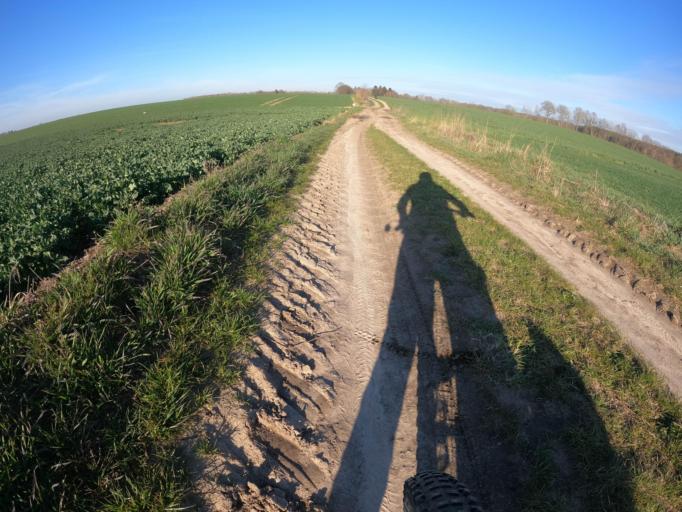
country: PL
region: West Pomeranian Voivodeship
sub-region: Powiat kolobrzeski
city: Ryman
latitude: 53.9801
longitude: 15.4475
